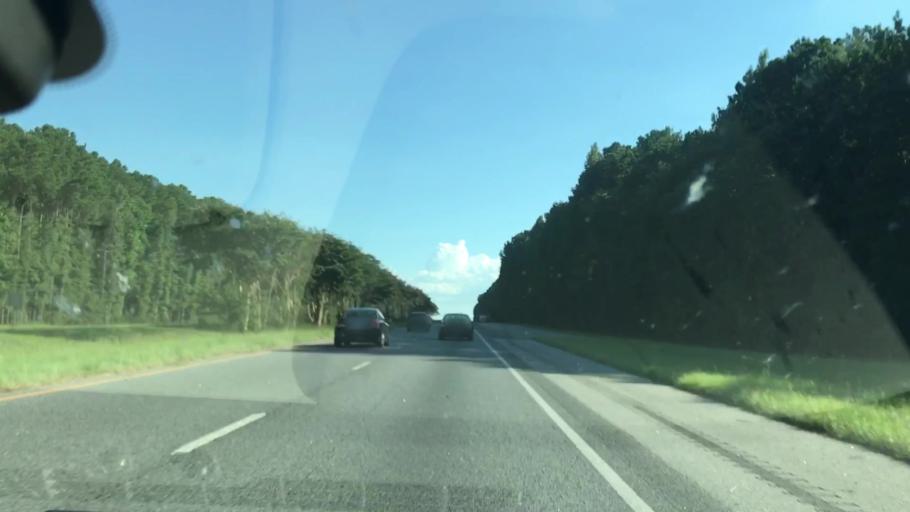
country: US
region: Georgia
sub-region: Harris County
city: Hamilton
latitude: 32.8114
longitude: -85.0214
